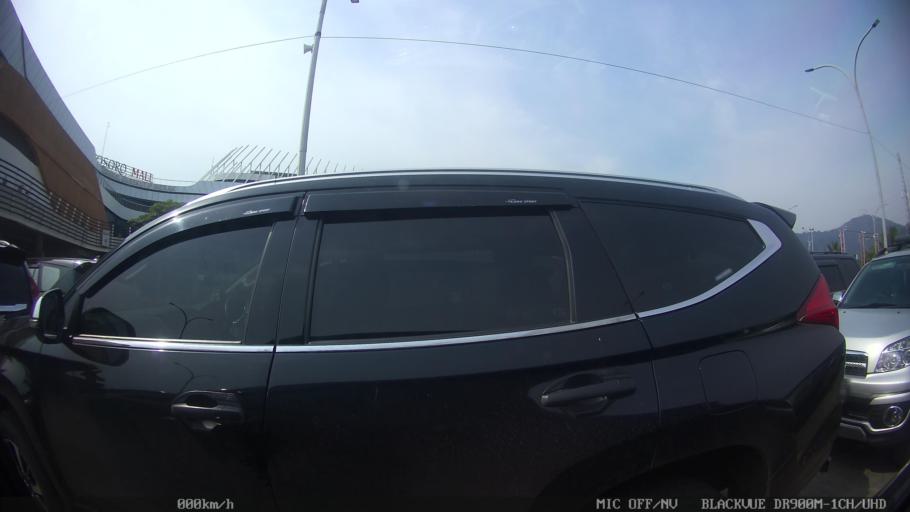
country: ID
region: Banten
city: Kubangkepuh
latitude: -5.9364
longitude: 105.9996
